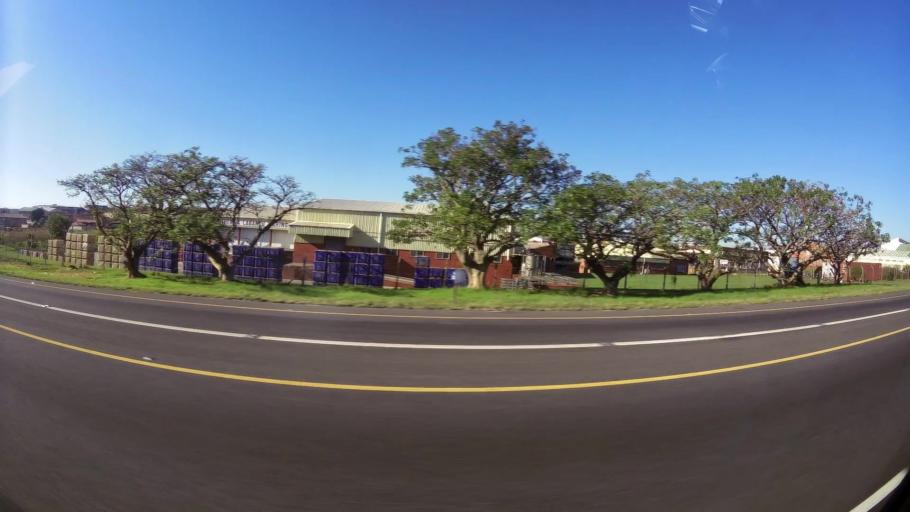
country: ZA
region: Eastern Cape
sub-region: Nelson Mandela Bay Metropolitan Municipality
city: Port Elizabeth
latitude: -33.9147
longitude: 25.5779
